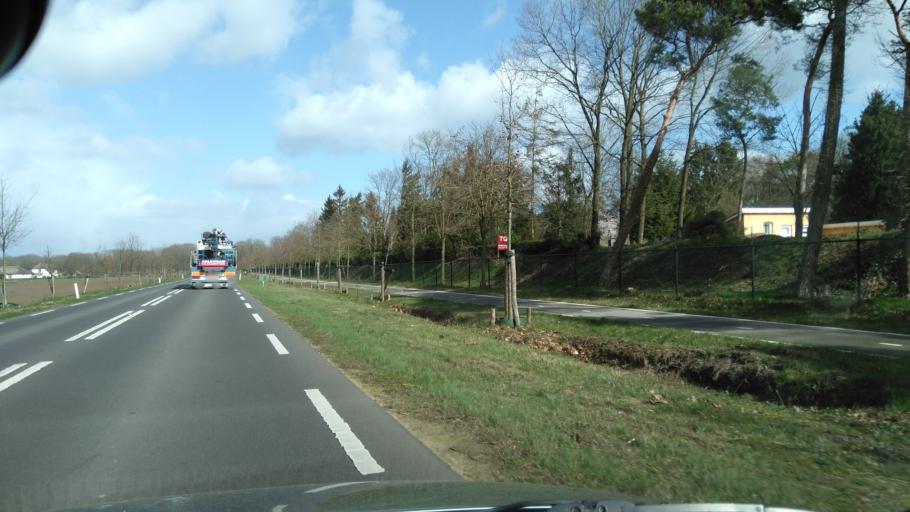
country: NL
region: North Brabant
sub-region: Gemeente Baarle-Nassau
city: Baarle-Nassau
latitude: 51.4169
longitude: 4.9347
